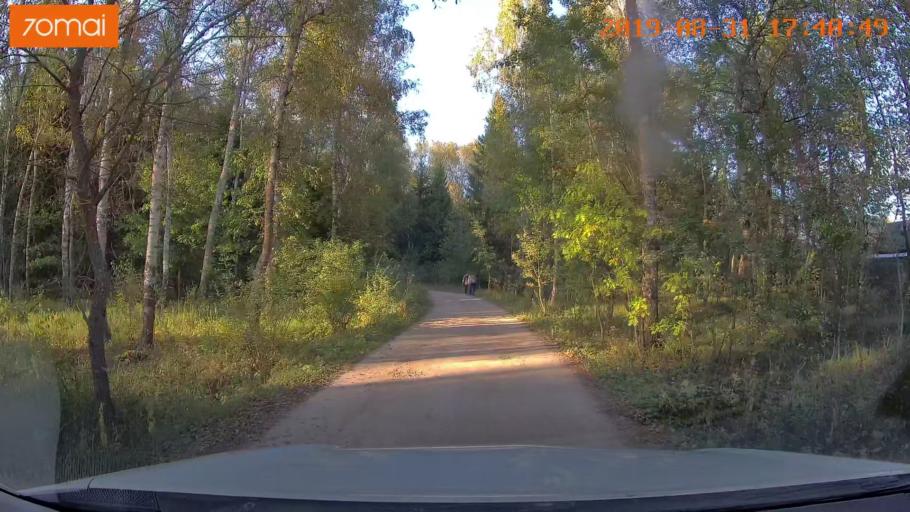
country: RU
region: Kaluga
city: Detchino
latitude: 54.8200
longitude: 36.3655
